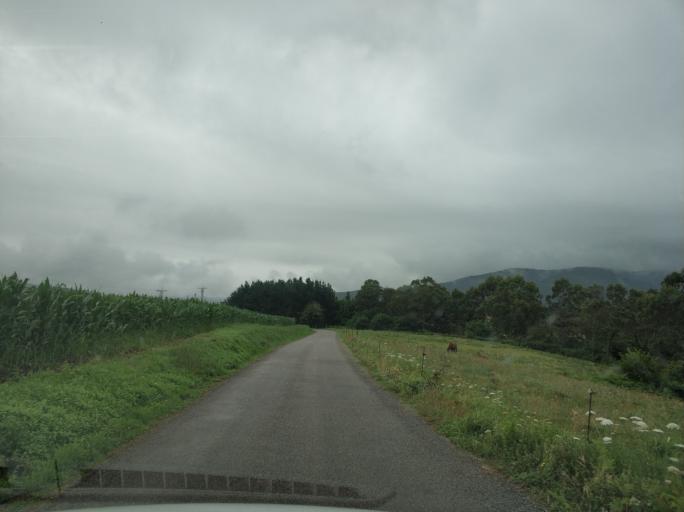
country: ES
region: Asturias
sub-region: Province of Asturias
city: Tineo
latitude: 43.5596
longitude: -6.4679
